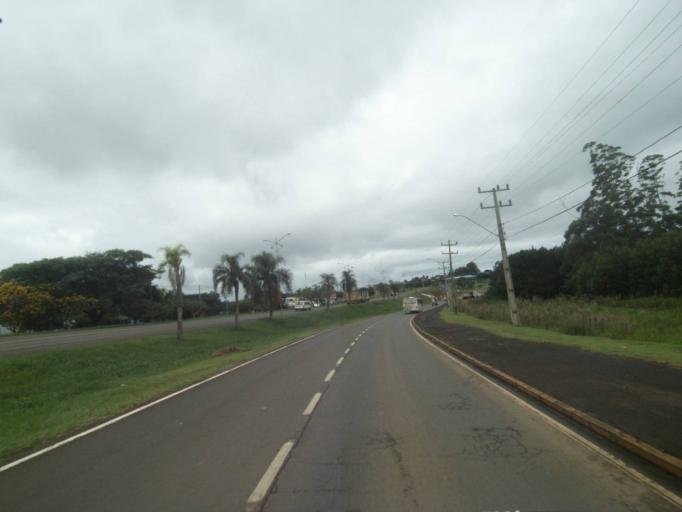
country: BR
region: Parana
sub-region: Telemaco Borba
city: Telemaco Borba
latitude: -24.3343
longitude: -50.6541
